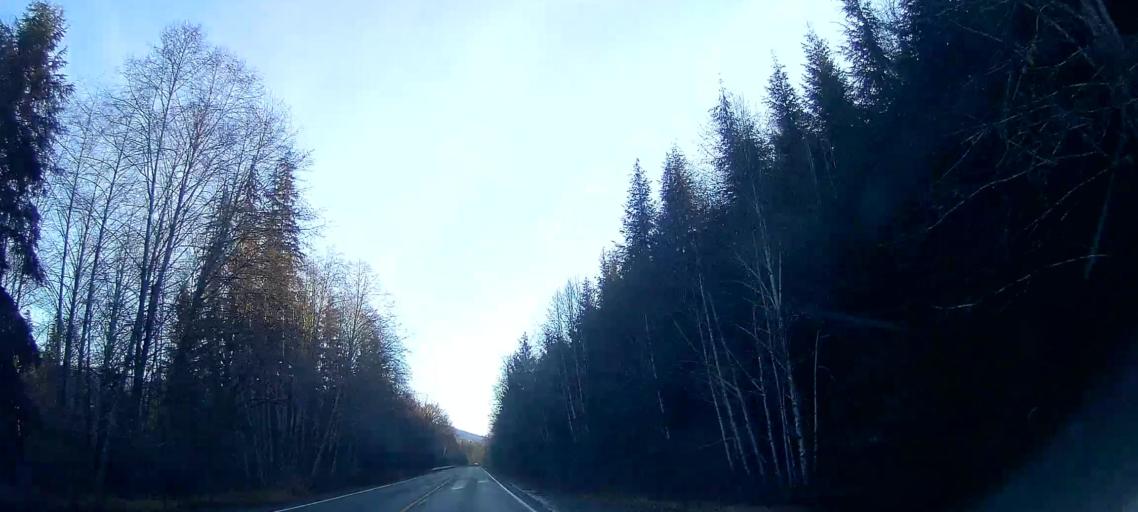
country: US
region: Washington
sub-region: Snohomish County
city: Darrington
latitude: 48.6322
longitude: -121.7401
